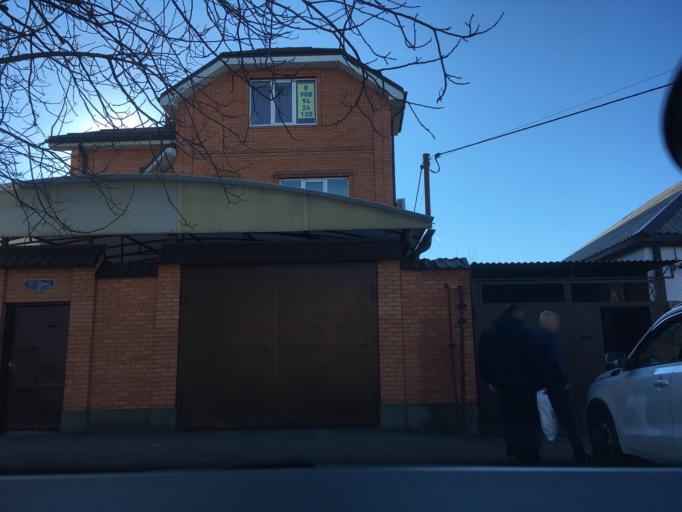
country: RU
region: Rostov
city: Imeni Chkalova
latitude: 47.2715
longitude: 39.7902
